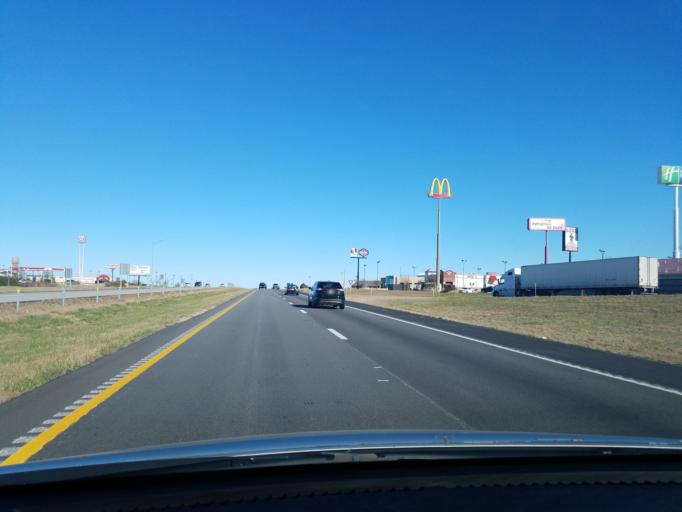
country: US
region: Missouri
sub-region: Webster County
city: Marshfield
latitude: 37.3432
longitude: -92.9299
